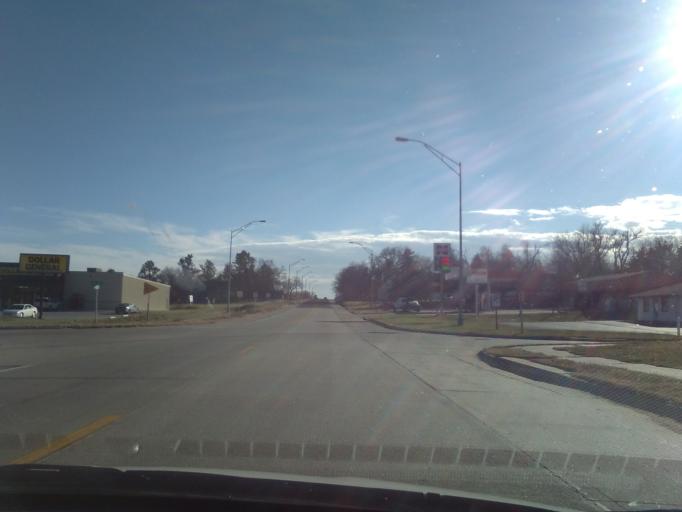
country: US
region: Nebraska
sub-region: Adams County
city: Hastings
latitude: 40.3359
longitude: -98.4439
